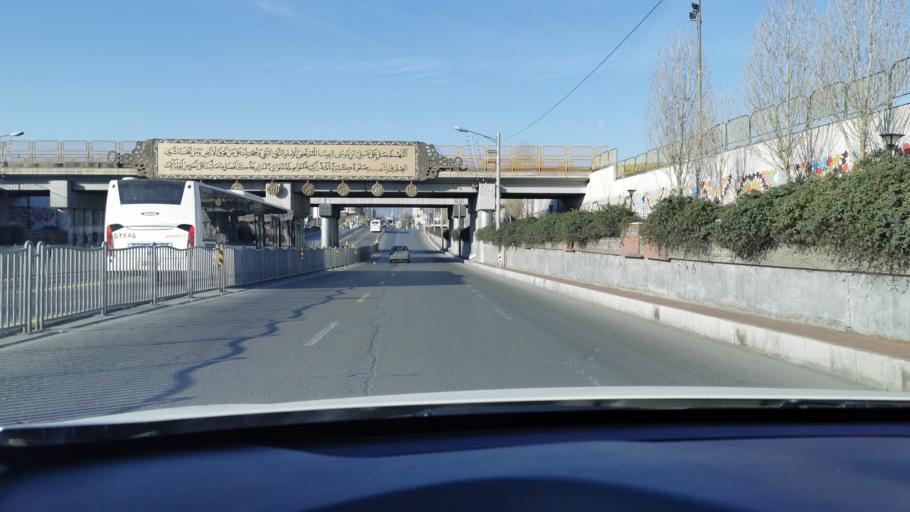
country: IR
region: Razavi Khorasan
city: Mashhad
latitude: 36.2978
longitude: 59.6312
